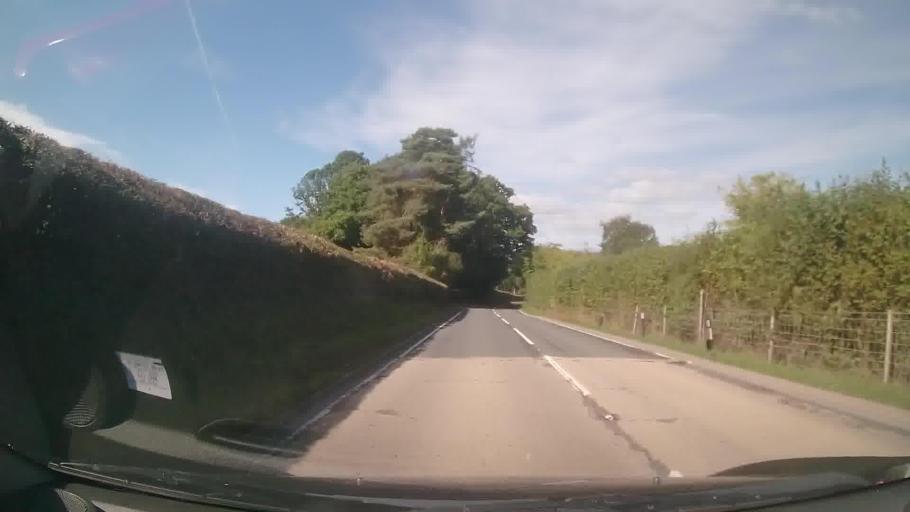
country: GB
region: England
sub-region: Herefordshire
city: Kington
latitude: 52.1911
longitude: -3.0186
